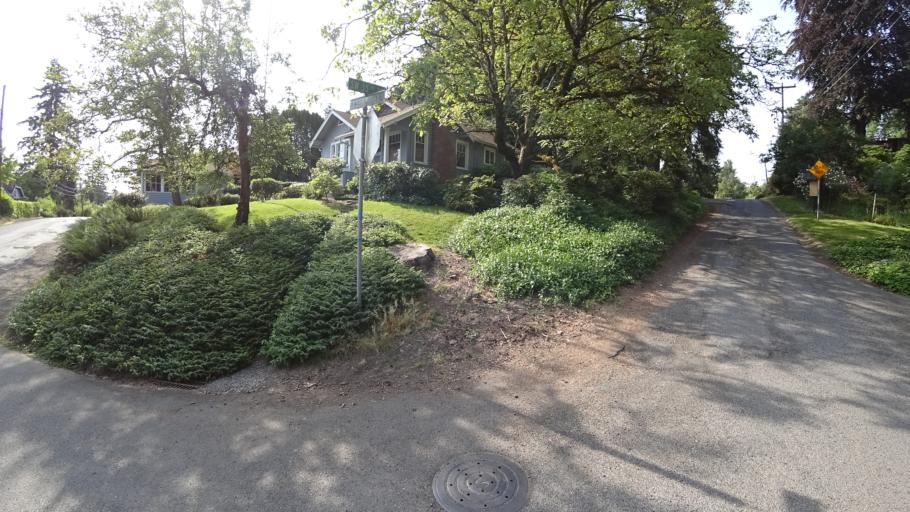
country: US
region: Oregon
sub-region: Washington County
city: Garden Home-Whitford
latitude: 45.4635
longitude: -122.7129
